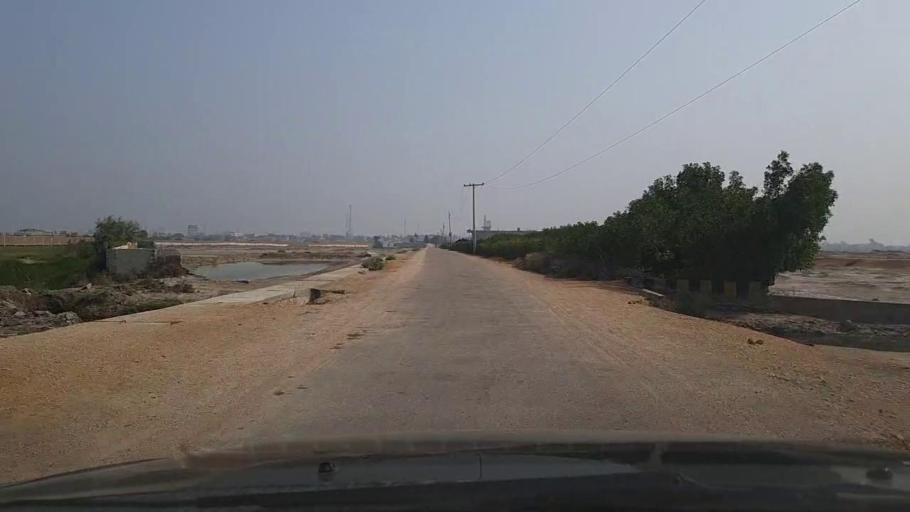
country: PK
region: Sindh
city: Thatta
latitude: 24.7455
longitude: 67.9095
